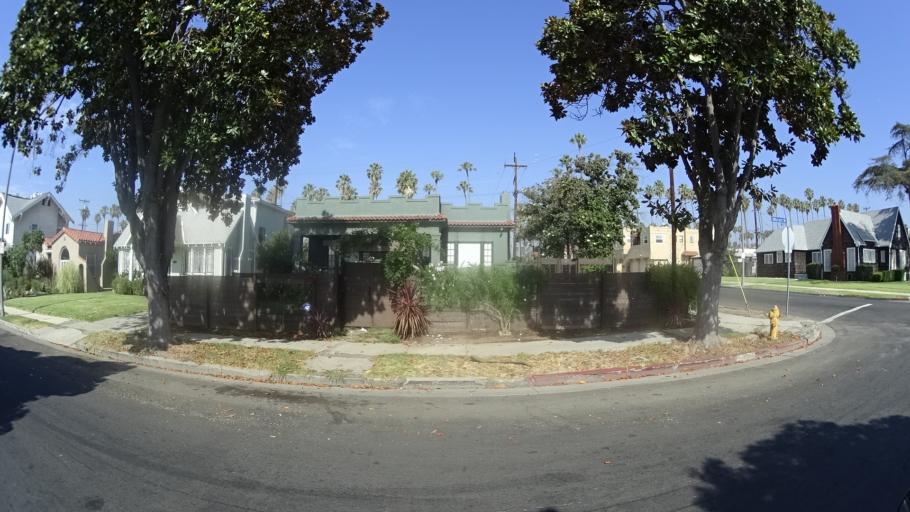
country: US
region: California
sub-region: Los Angeles County
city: View Park-Windsor Hills
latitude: 33.9906
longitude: -118.3369
